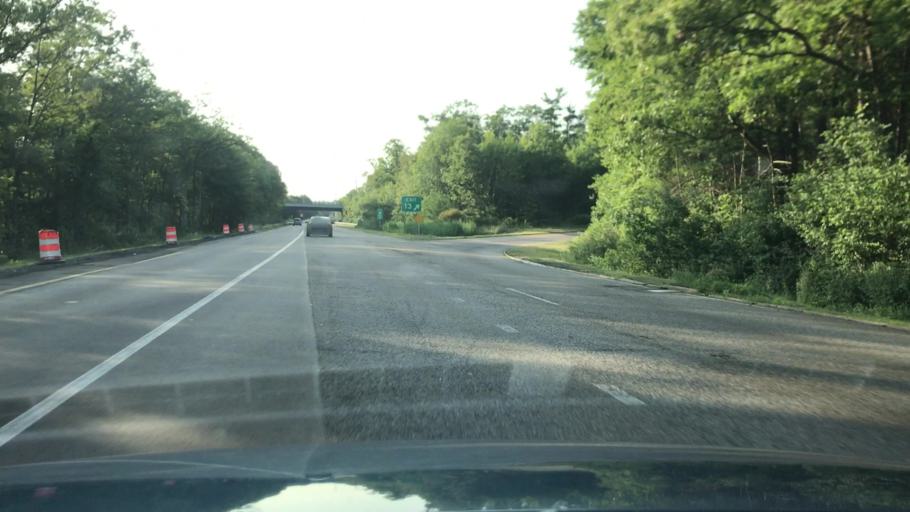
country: US
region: Massachusetts
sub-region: Plymouth County
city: Hanover
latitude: 42.1524
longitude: -70.8490
